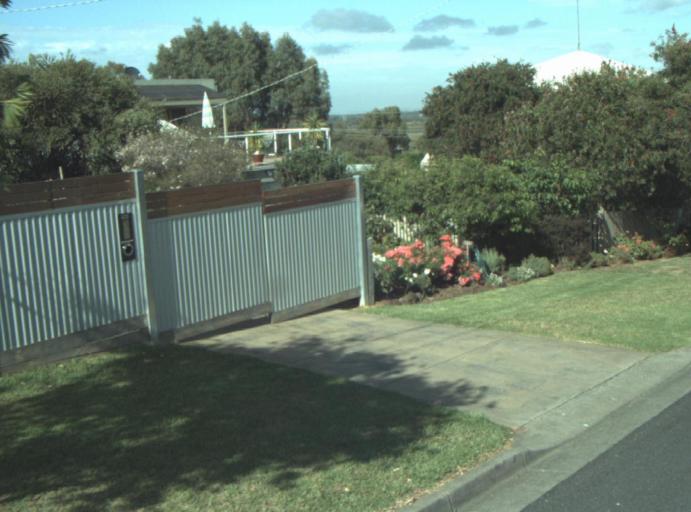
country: AU
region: Victoria
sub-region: Greater Geelong
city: Leopold
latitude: -38.2543
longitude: 144.5078
